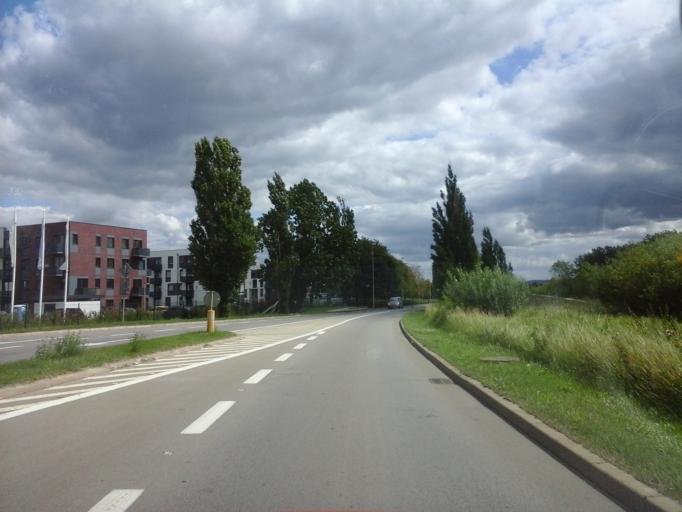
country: PL
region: West Pomeranian Voivodeship
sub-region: Powiat policki
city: Przeclaw
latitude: 53.3938
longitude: 14.4914
